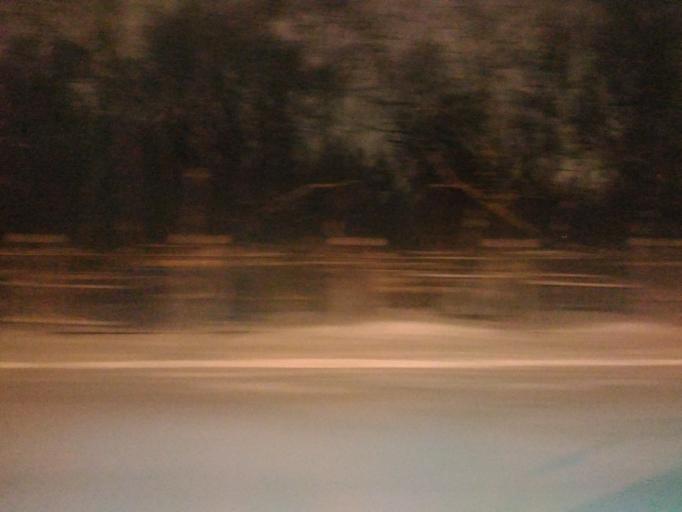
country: RU
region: Ulyanovsk
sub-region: Ulyanovskiy Rayon
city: Ulyanovsk
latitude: 54.3253
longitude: 48.3697
